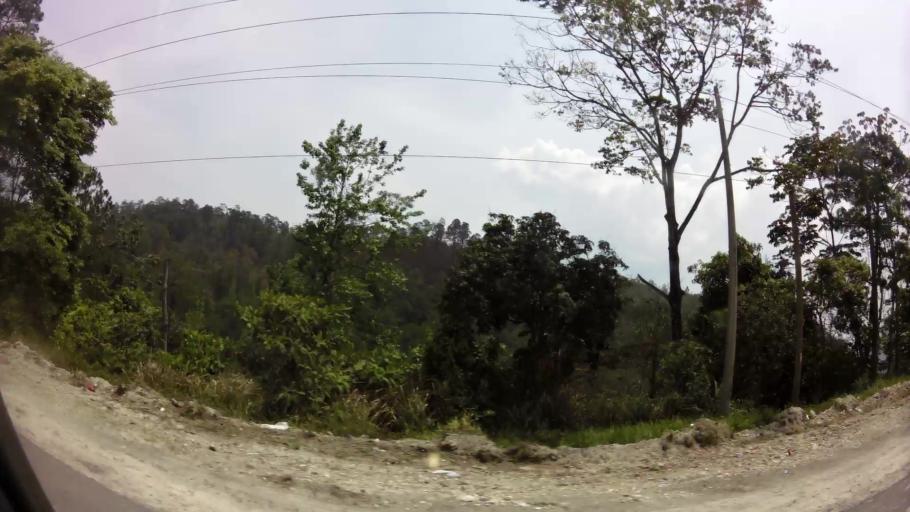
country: HN
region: Comayagua
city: El Socorro
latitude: 14.6544
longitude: -87.9381
